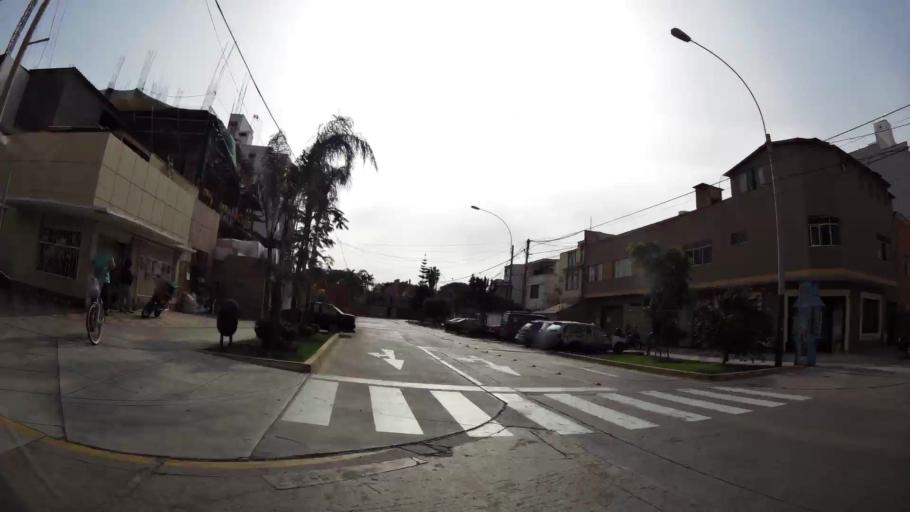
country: PE
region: Lima
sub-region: Lima
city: San Isidro
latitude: -12.0951
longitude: -77.0617
